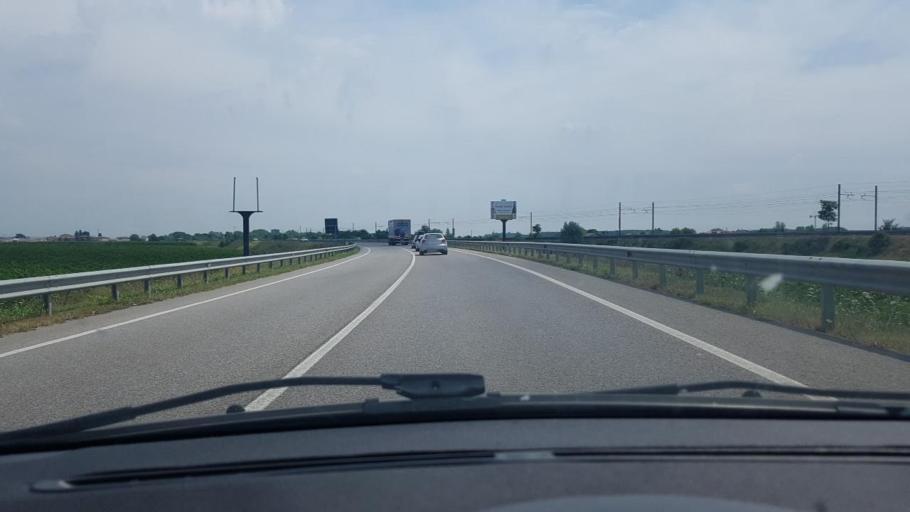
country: IT
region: Veneto
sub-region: Provincia di Verona
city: Peschiera del Garda
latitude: 45.4413
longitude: 10.6500
